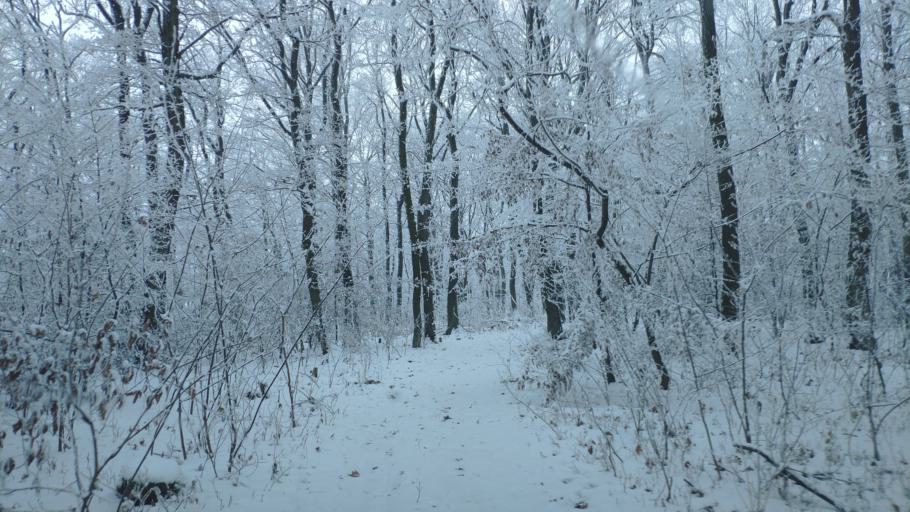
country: SK
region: Kosicky
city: Kosice
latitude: 48.6531
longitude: 21.1831
